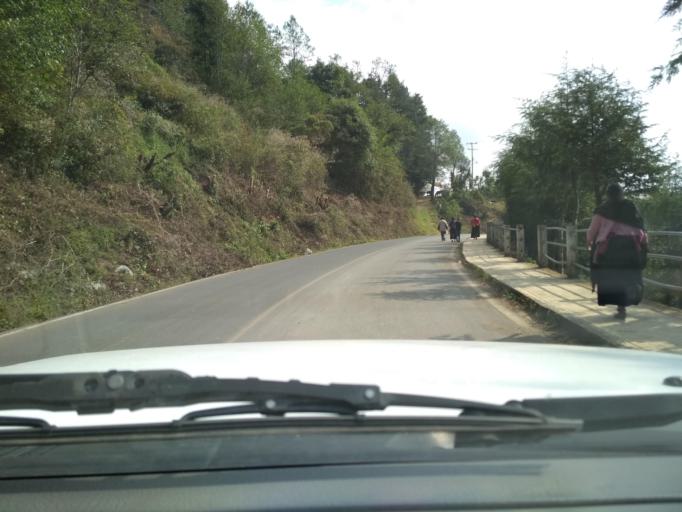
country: MX
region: Veracruz
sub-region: Soledad Atzompa
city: Tlatilpa
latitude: 18.7518
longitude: -97.1544
